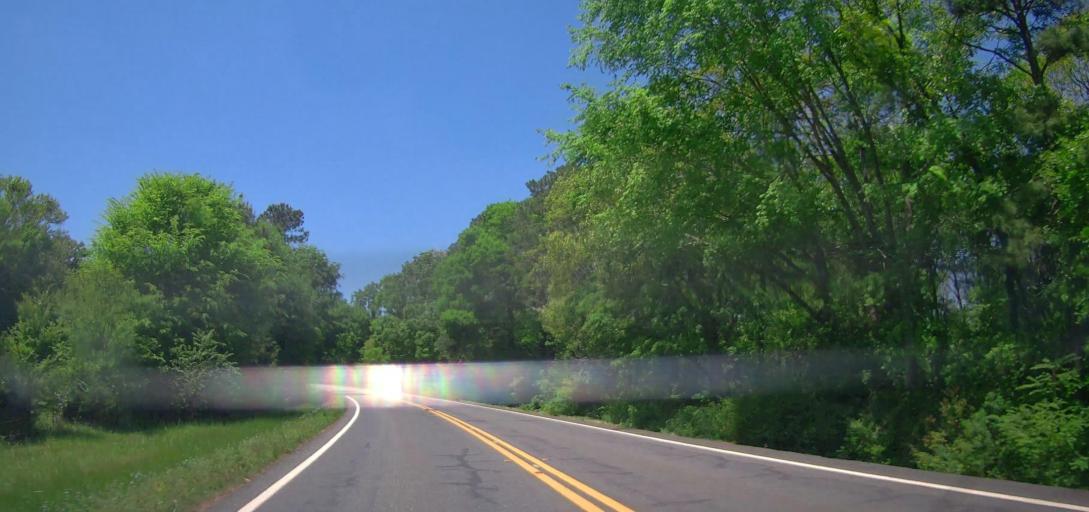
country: US
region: Georgia
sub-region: Jasper County
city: Monticello
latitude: 33.2819
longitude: -83.6198
